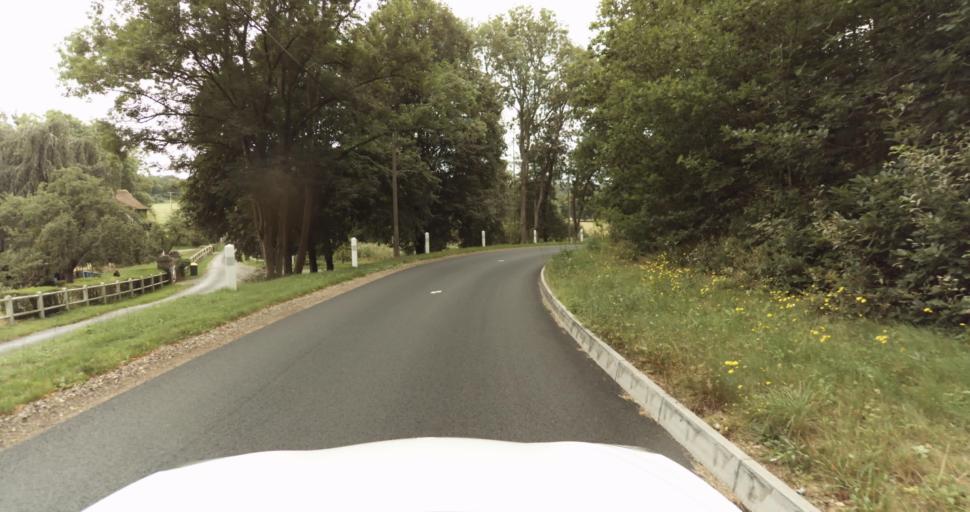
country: FR
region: Haute-Normandie
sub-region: Departement de l'Eure
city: Damville
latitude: 48.9258
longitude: 1.0673
